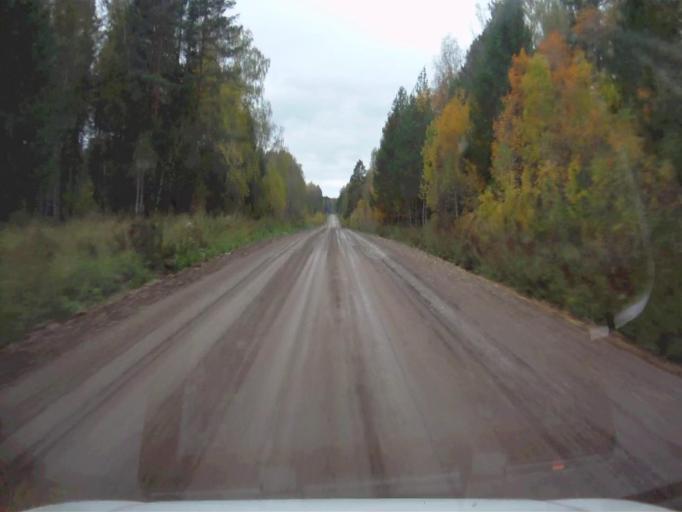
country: RU
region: Chelyabinsk
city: Nyazepetrovsk
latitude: 56.0924
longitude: 59.4098
